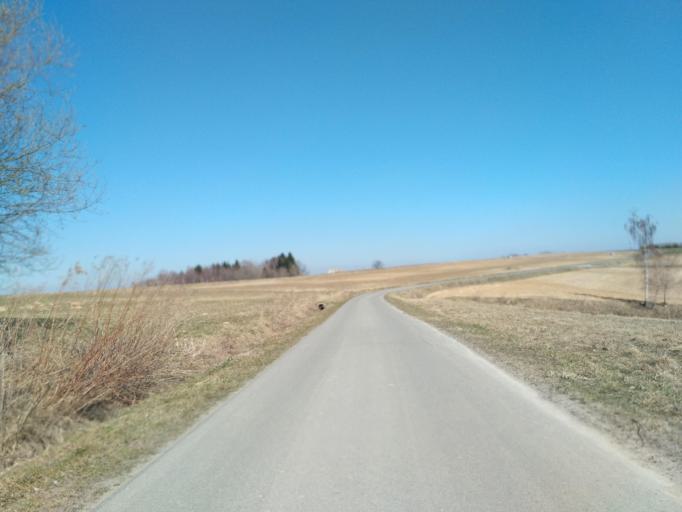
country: PL
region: Subcarpathian Voivodeship
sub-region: Powiat ropczycko-sedziszowski
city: Niedzwiada
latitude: 49.9529
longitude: 21.5347
